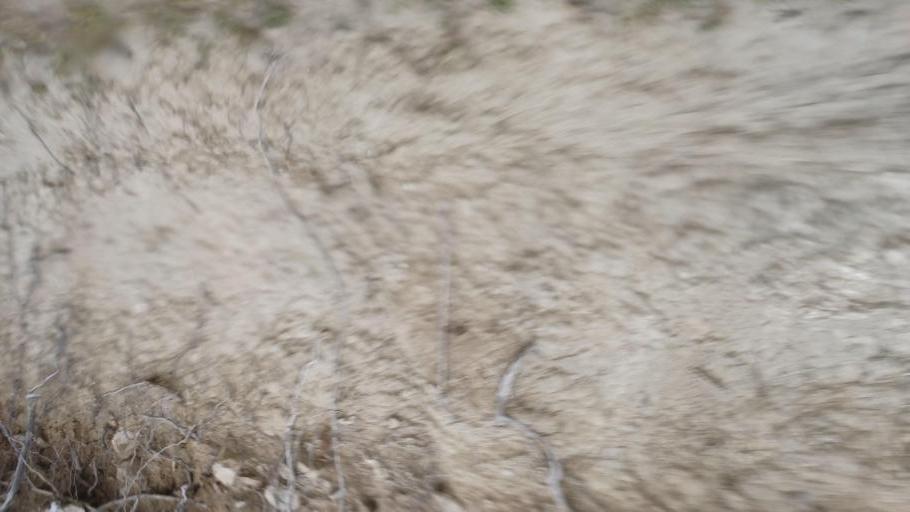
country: CY
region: Limassol
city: Pelendri
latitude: 34.8628
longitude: 33.0891
